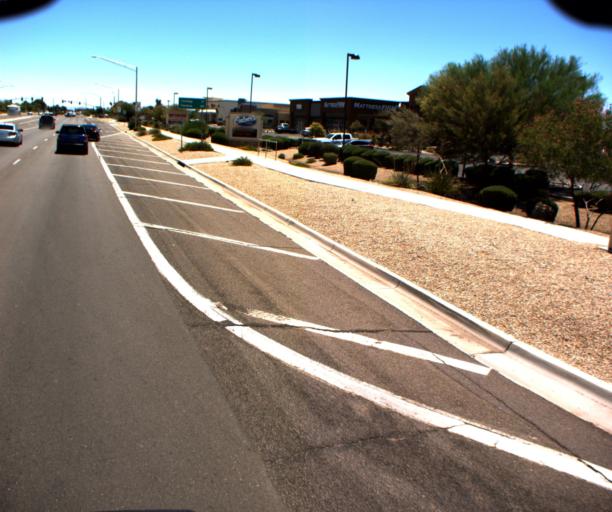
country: US
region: Arizona
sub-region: Pinal County
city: Casa Grande
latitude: 32.8796
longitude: -111.6823
